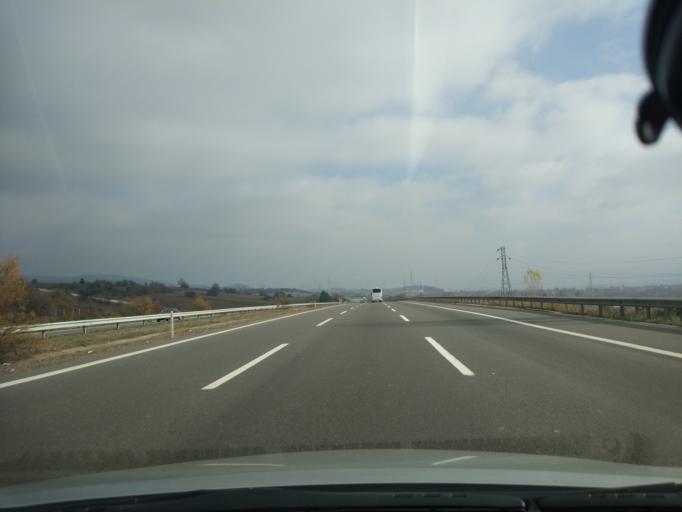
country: TR
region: Bolu
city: Bolu
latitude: 40.7639
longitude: 31.6149
